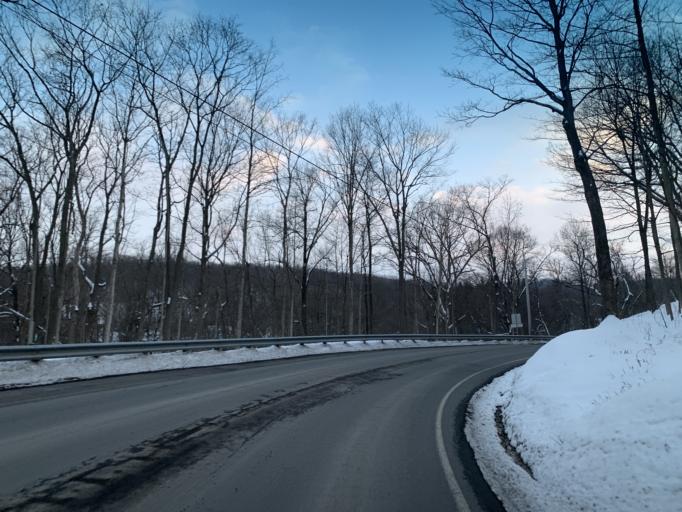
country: US
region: Maryland
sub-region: Allegany County
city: Frostburg
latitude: 39.6819
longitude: -78.8902
